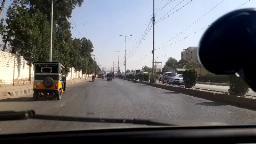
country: PK
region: Sindh
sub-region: Karachi District
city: Karachi
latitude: 24.8935
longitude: 67.0858
